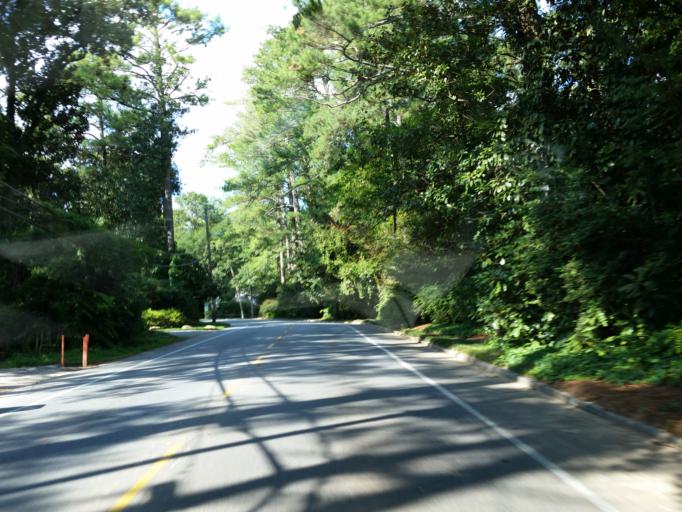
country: US
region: Georgia
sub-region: Cobb County
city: Vinings
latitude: 33.8588
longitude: -84.4036
